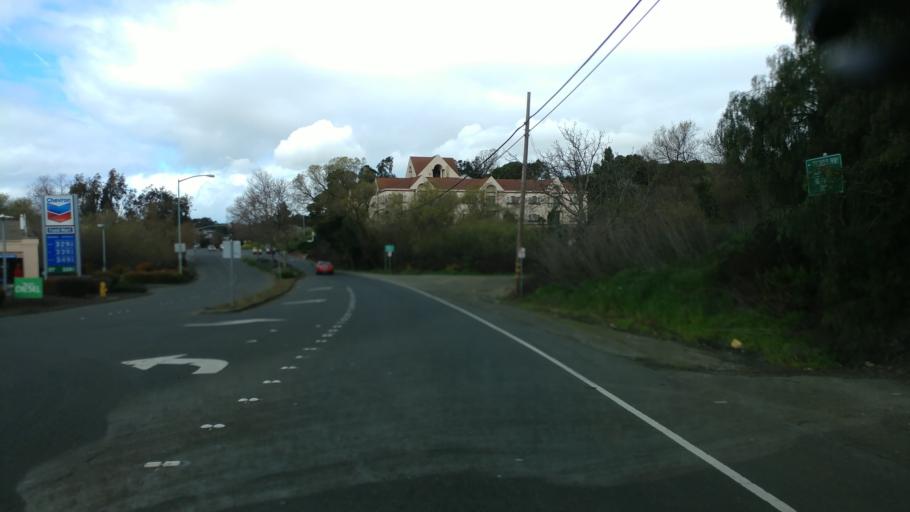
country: US
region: California
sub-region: Contra Costa County
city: Crockett
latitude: 38.0799
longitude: -122.1906
